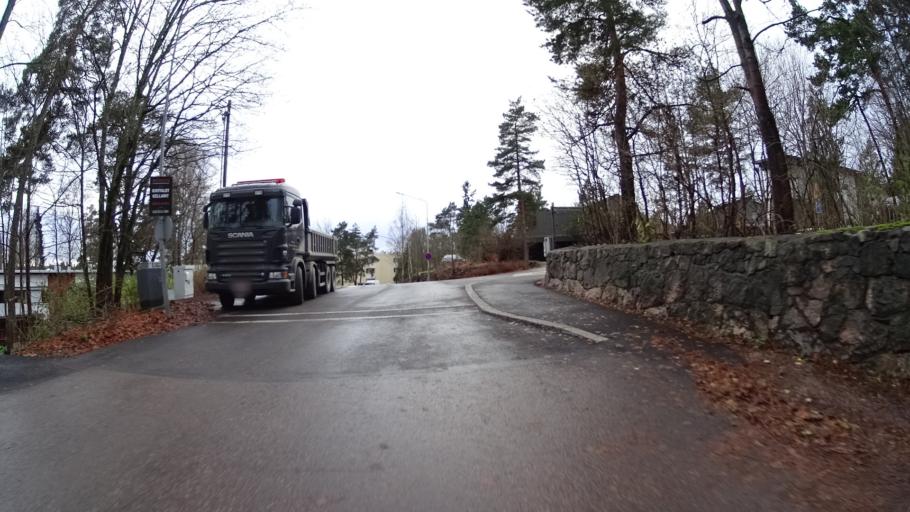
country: FI
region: Uusimaa
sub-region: Helsinki
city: Kauniainen
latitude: 60.2143
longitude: 24.7283
